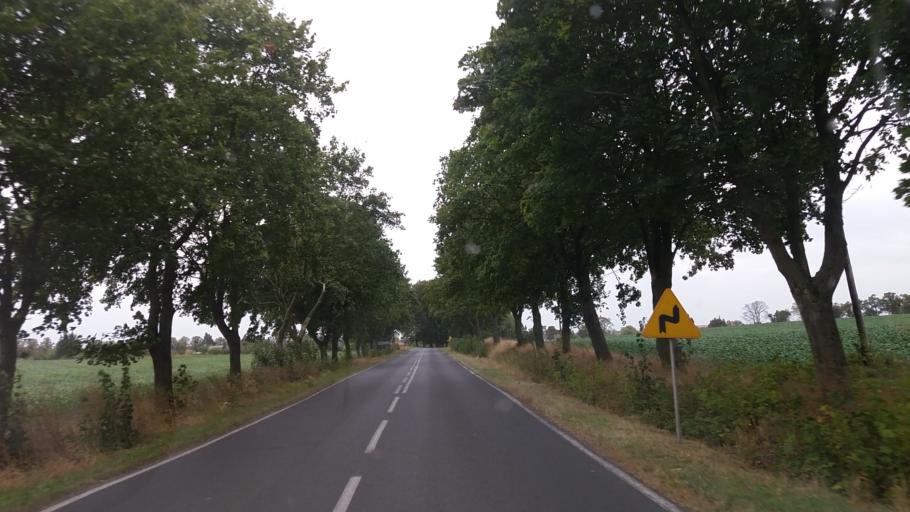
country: PL
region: Lubusz
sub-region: Powiat strzelecko-drezdenecki
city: Strzelce Krajenskie
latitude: 52.8878
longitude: 15.5412
